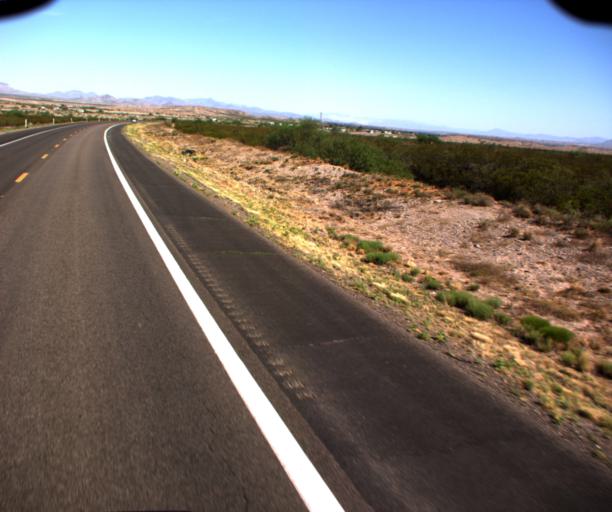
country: US
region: Arizona
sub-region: Greenlee County
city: Clifton
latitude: 32.6583
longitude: -109.0674
